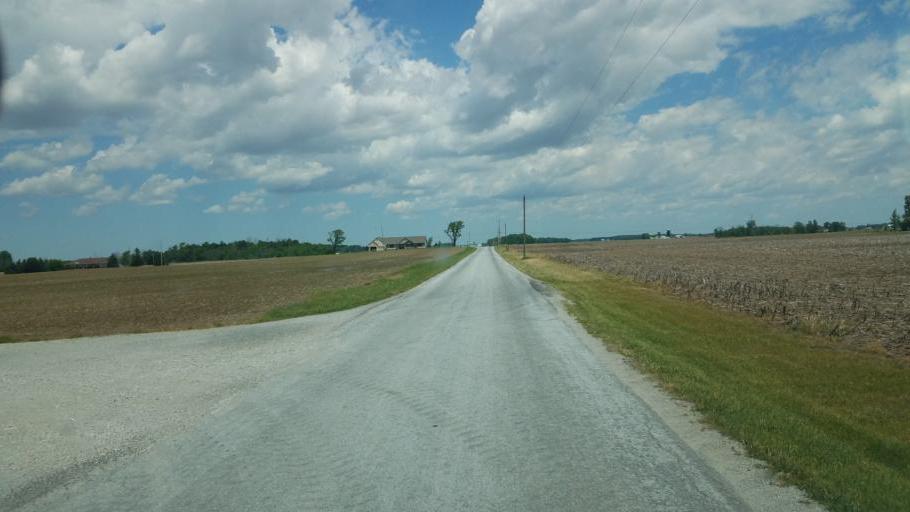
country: US
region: Ohio
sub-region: Hardin County
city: Kenton
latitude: 40.6550
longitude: -83.4773
